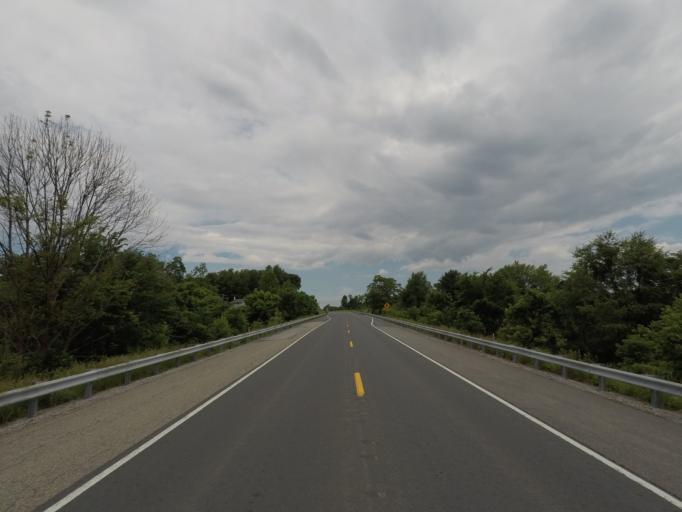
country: US
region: Maryland
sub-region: Washington County
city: Keedysville
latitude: 39.4103
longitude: -77.6615
